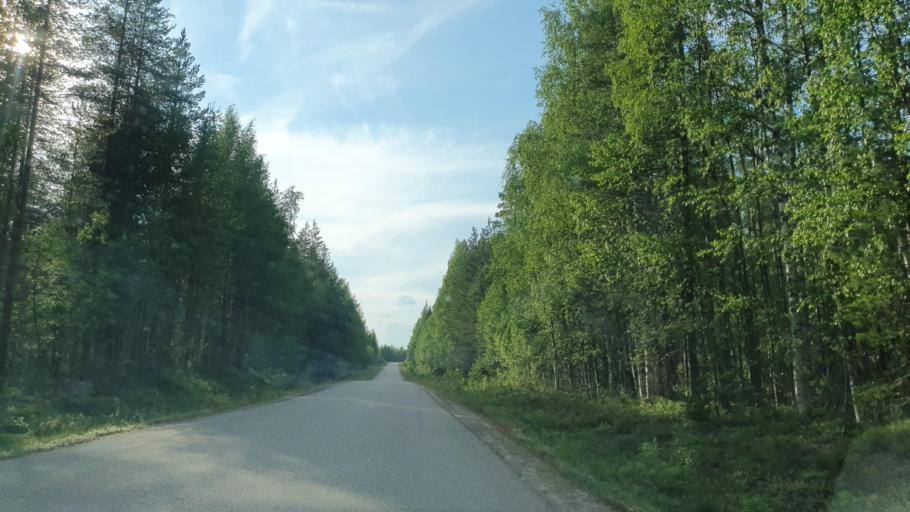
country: FI
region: Kainuu
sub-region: Kehys-Kainuu
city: Kuhmo
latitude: 64.2835
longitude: 29.3923
